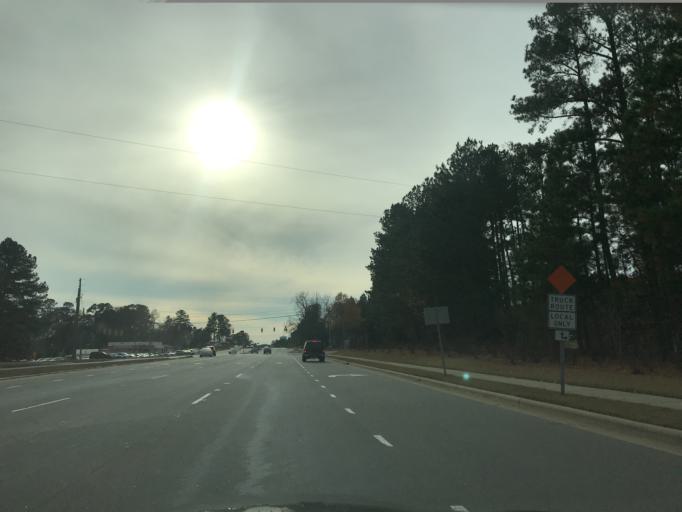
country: US
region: North Carolina
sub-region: Wake County
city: Knightdale
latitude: 35.8568
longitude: -78.5541
